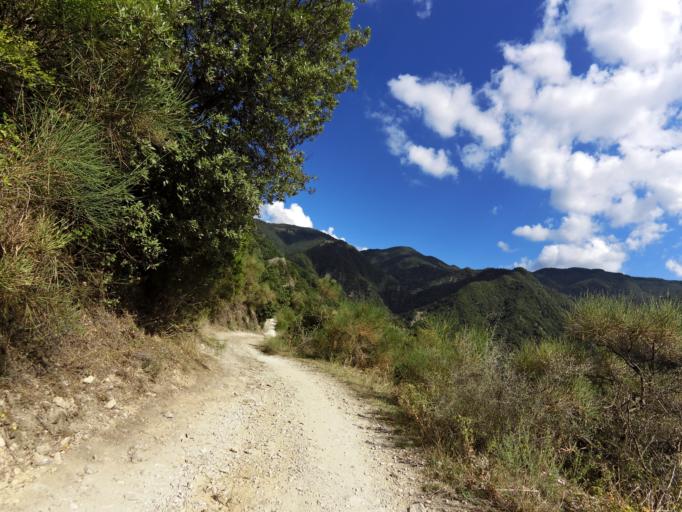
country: IT
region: Calabria
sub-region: Provincia di Reggio Calabria
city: Bivongi
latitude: 38.4895
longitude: 16.4073
